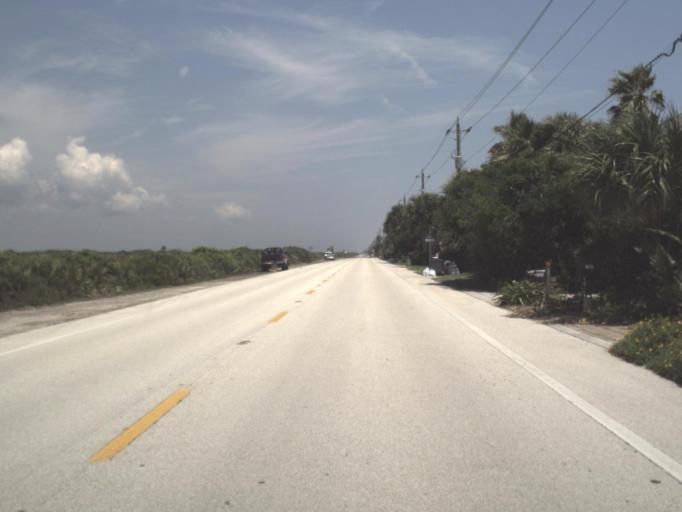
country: US
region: Florida
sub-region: Saint Johns County
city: Villano Beach
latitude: 30.0013
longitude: -81.3180
